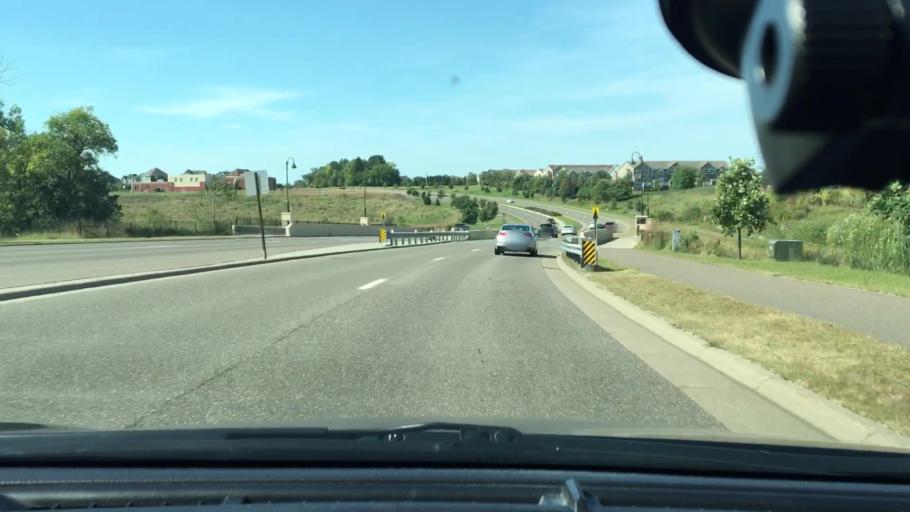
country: US
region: Minnesota
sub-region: Hennepin County
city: Maple Grove
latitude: 45.0843
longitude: -93.4909
